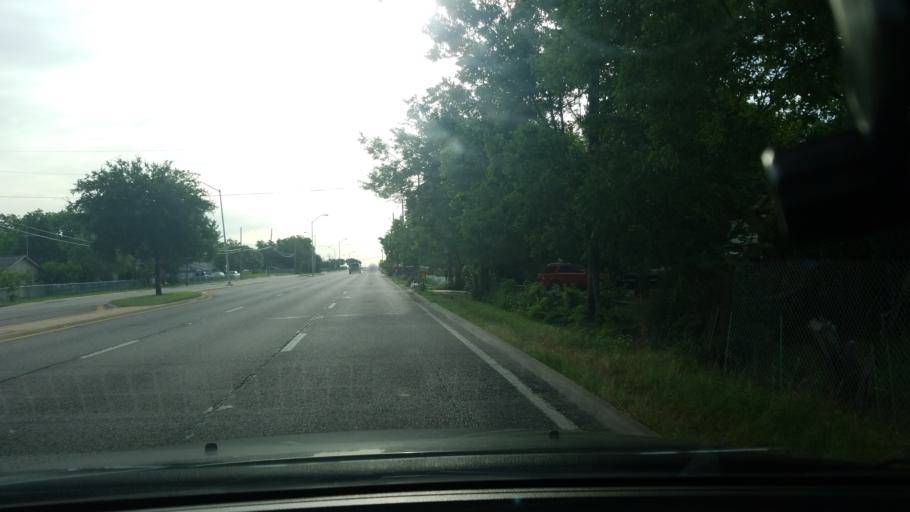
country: US
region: Texas
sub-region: Dallas County
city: Balch Springs
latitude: 32.7632
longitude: -96.6411
